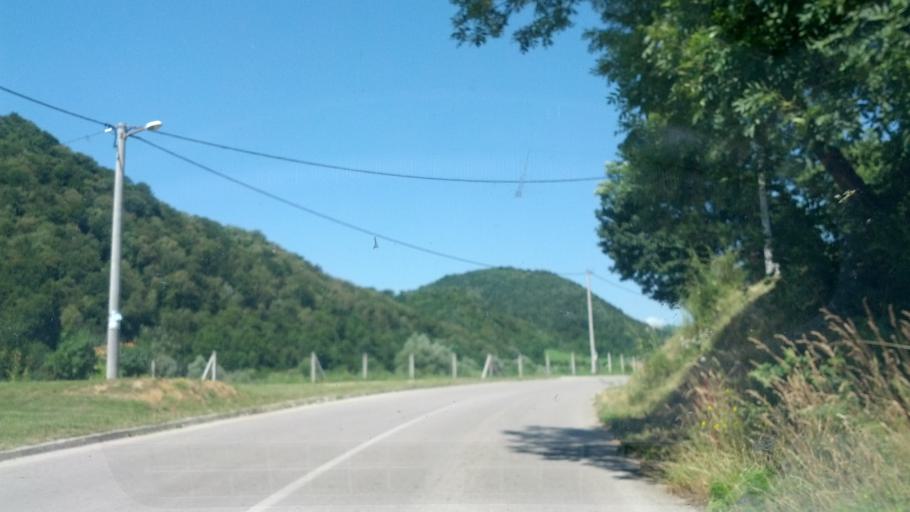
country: BA
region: Federation of Bosnia and Herzegovina
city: Otoka
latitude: 44.9964
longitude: 16.1531
